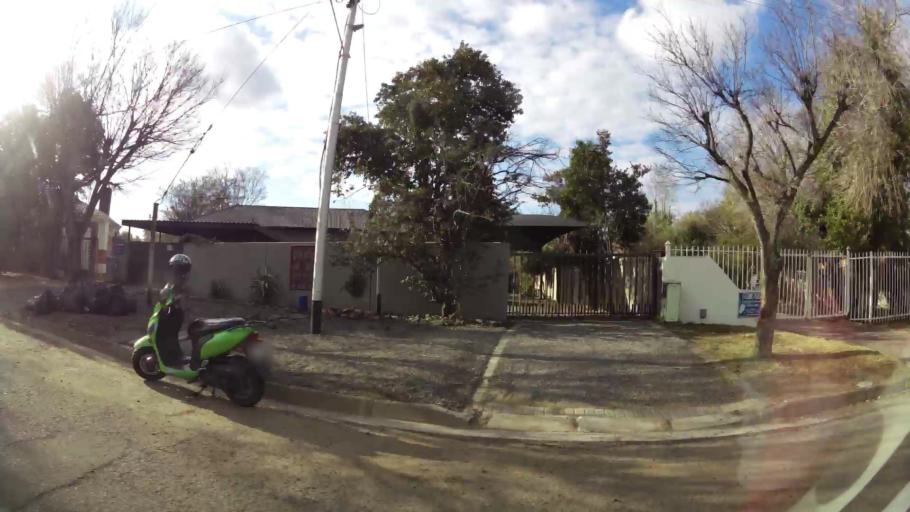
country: ZA
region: Orange Free State
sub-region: Mangaung Metropolitan Municipality
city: Bloemfontein
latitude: -29.0814
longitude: 26.2102
